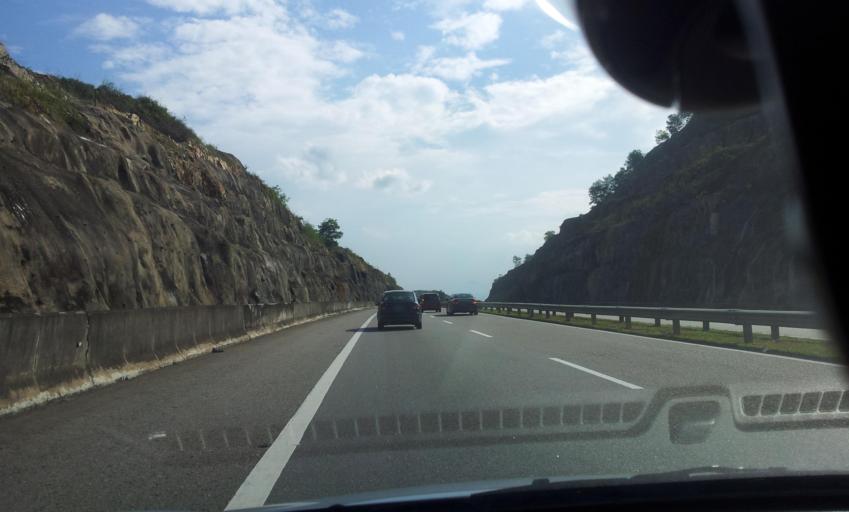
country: MY
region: Pahang
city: Mentekab
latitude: 3.5142
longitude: 102.1380
